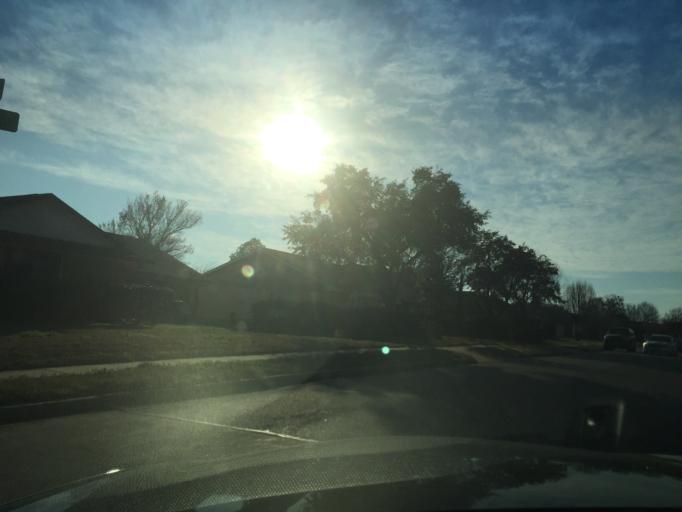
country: US
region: Texas
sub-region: Dallas County
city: Carrollton
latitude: 32.9870
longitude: -96.8801
